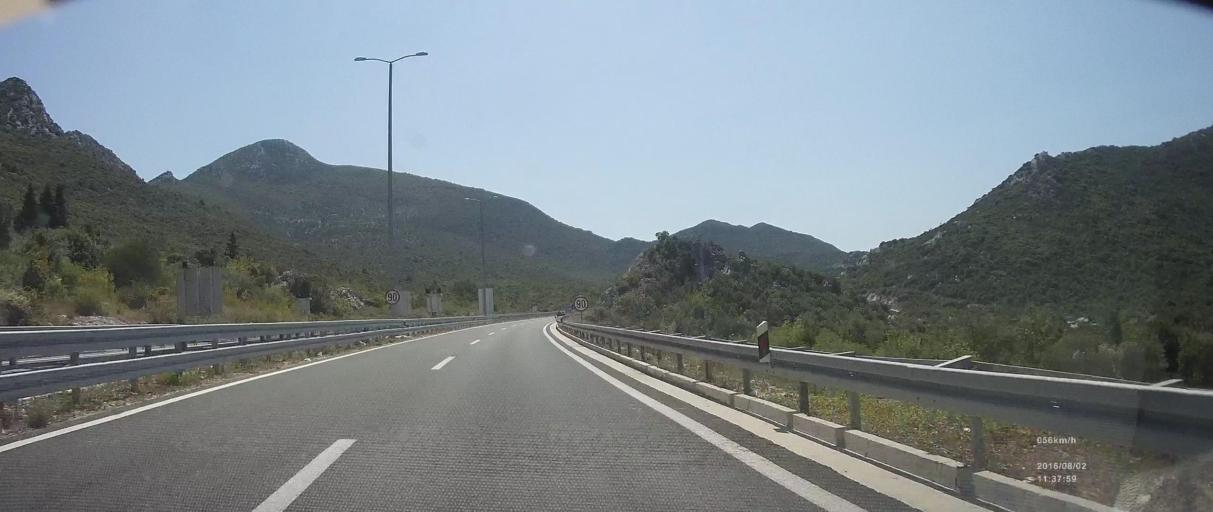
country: HR
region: Dubrovacko-Neretvanska
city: Komin
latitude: 43.1001
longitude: 17.4877
